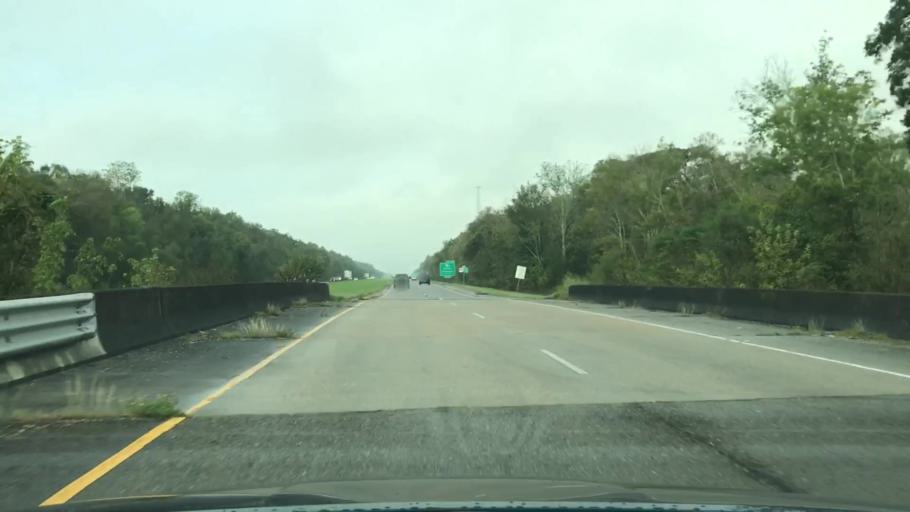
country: US
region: Louisiana
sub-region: Terrebonne Parish
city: Gray
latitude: 29.6820
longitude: -90.7599
